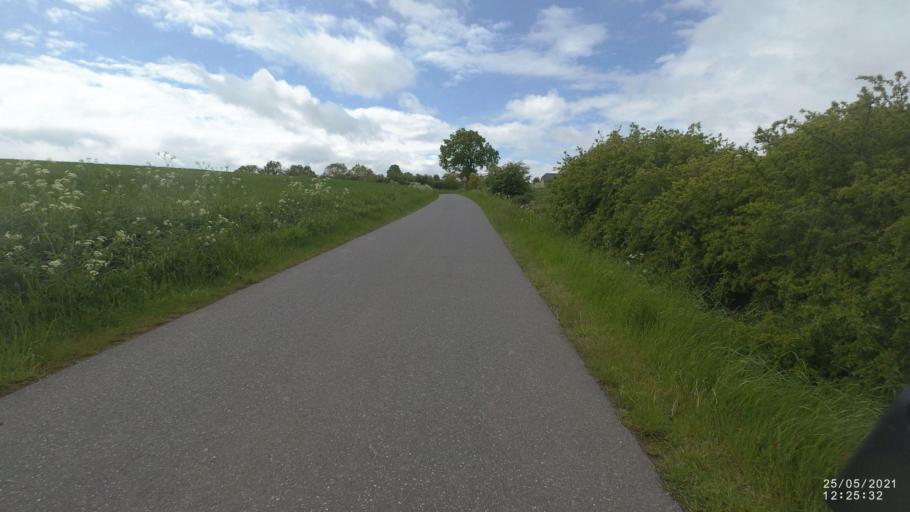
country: DE
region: Rheinland-Pfalz
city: Mayen
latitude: 50.3123
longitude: 7.2072
